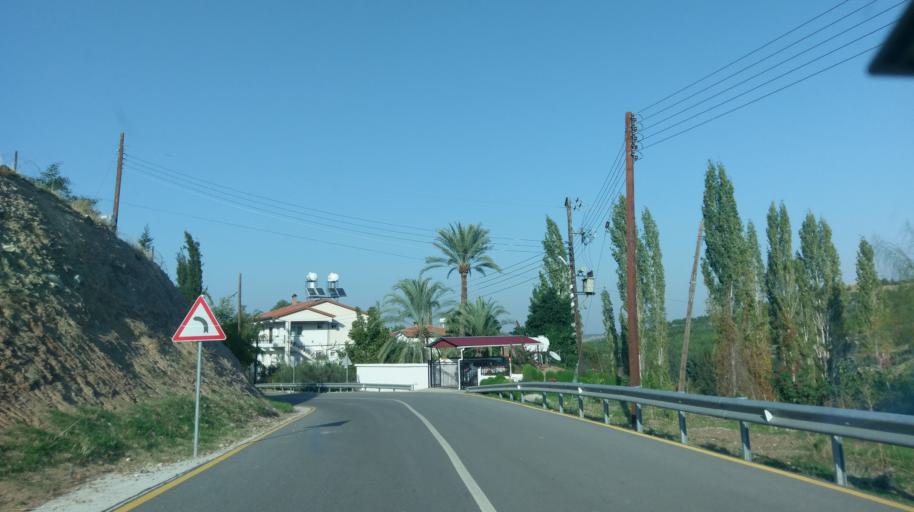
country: CY
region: Lefkosia
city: Lefka
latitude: 35.0895
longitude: 32.8430
